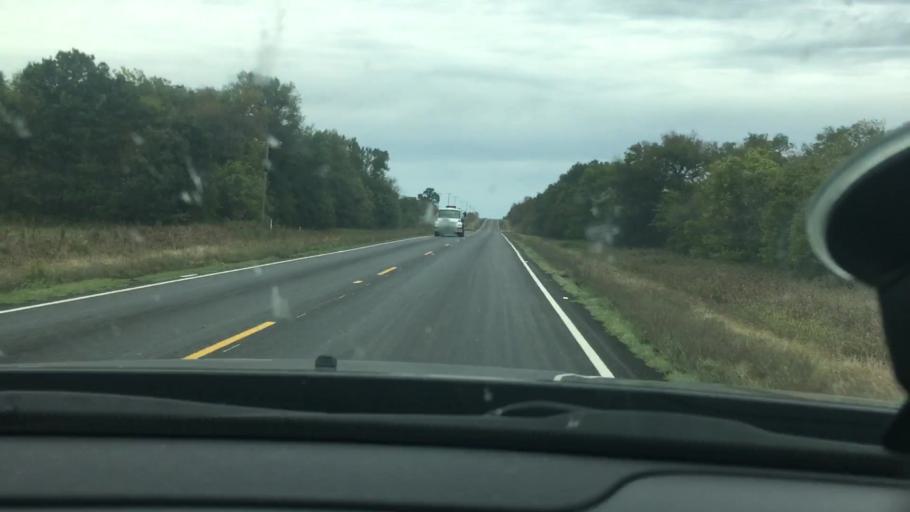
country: US
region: Oklahoma
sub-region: Coal County
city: Coalgate
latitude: 34.4046
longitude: -96.4245
